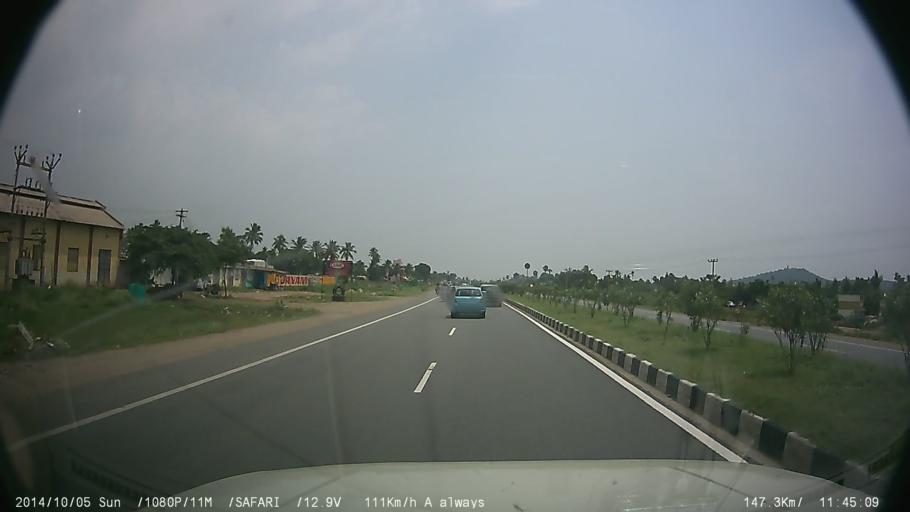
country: IN
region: Tamil Nadu
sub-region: Salem
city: Attur
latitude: 11.5922
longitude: 78.6487
